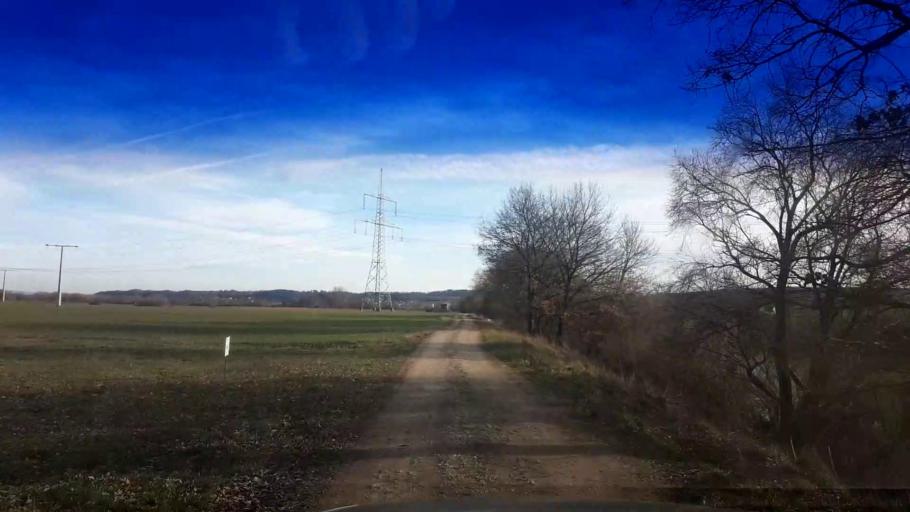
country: DE
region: Bavaria
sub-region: Upper Franconia
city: Viereth-Trunstadt
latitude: 49.9427
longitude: 10.7477
